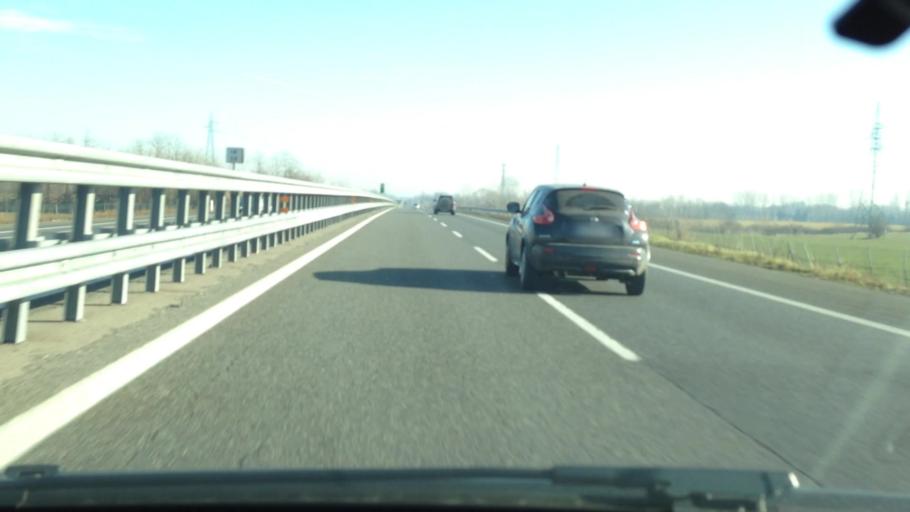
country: IT
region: Piedmont
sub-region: Provincia di Alessandria
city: Solero
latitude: 44.9244
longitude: 8.4966
